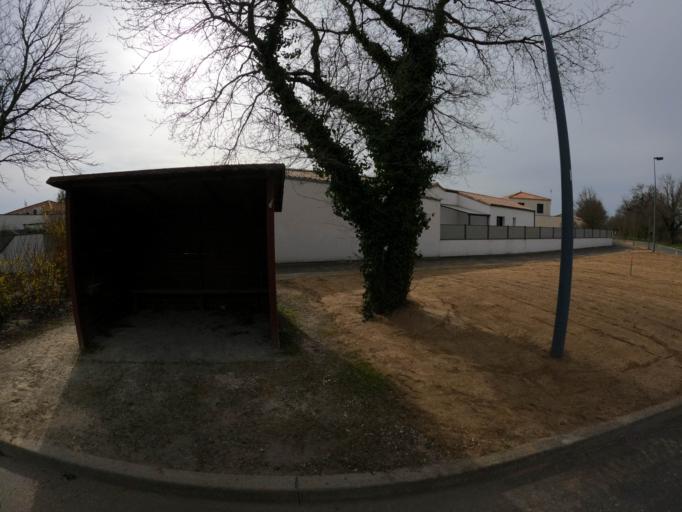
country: FR
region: Pays de la Loire
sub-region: Departement de la Vendee
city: Bouffere
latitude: 46.9656
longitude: -1.3301
